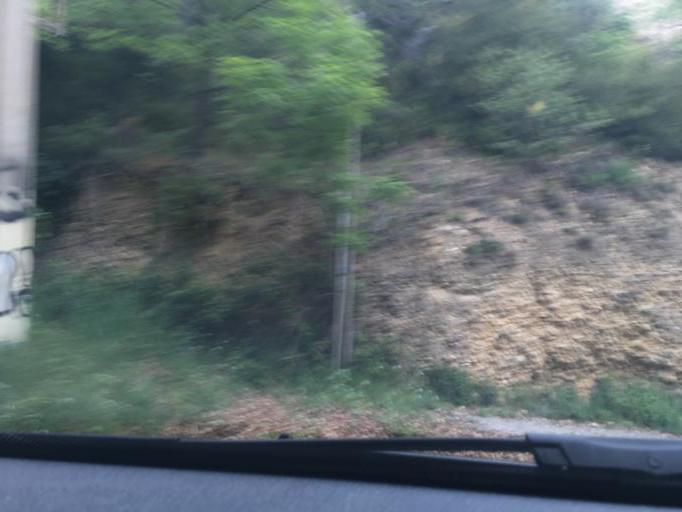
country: FR
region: Provence-Alpes-Cote d'Azur
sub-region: Departement des Alpes-de-Haute-Provence
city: Riez
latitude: 43.7579
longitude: 6.1508
